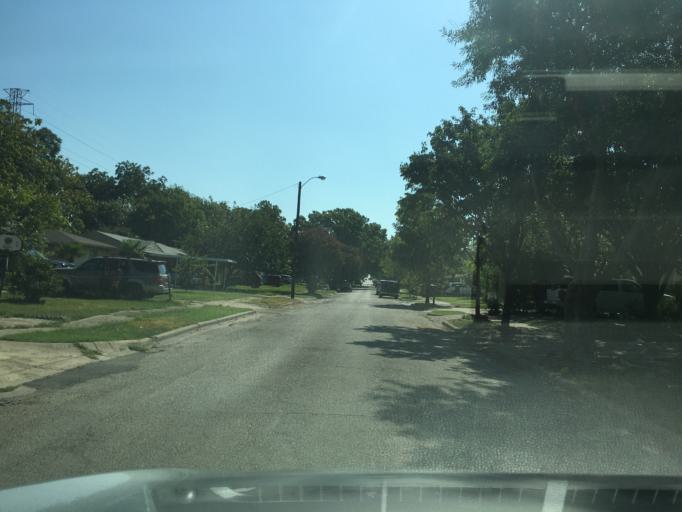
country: US
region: Texas
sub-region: Dallas County
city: Garland
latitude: 32.8550
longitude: -96.6757
